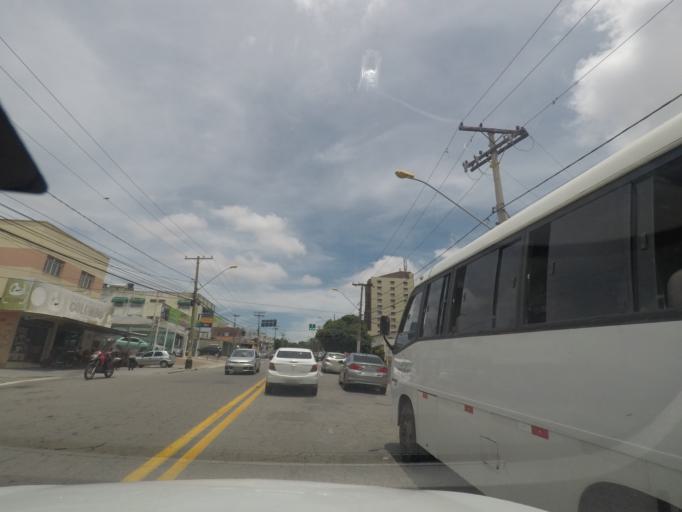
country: BR
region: Goias
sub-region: Goiania
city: Goiania
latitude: -16.6879
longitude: -49.2500
